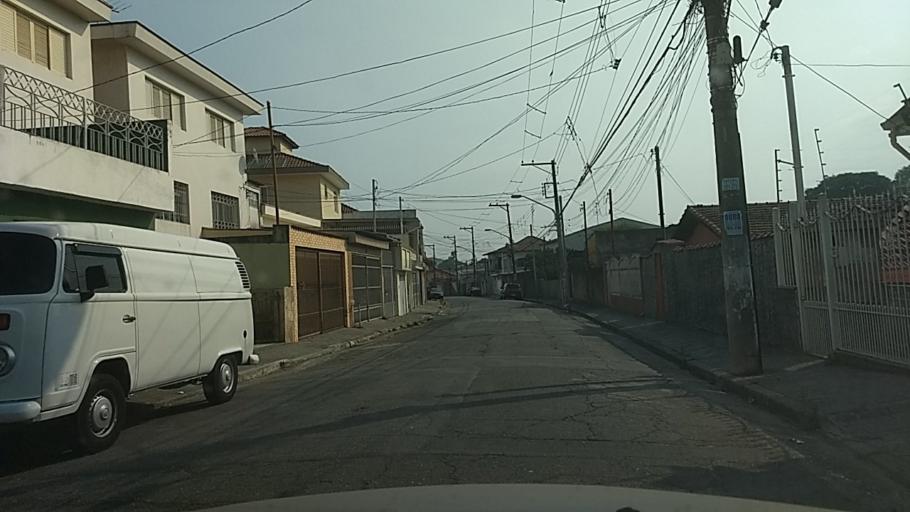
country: BR
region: Sao Paulo
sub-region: Sao Paulo
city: Sao Paulo
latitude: -23.5044
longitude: -46.5952
